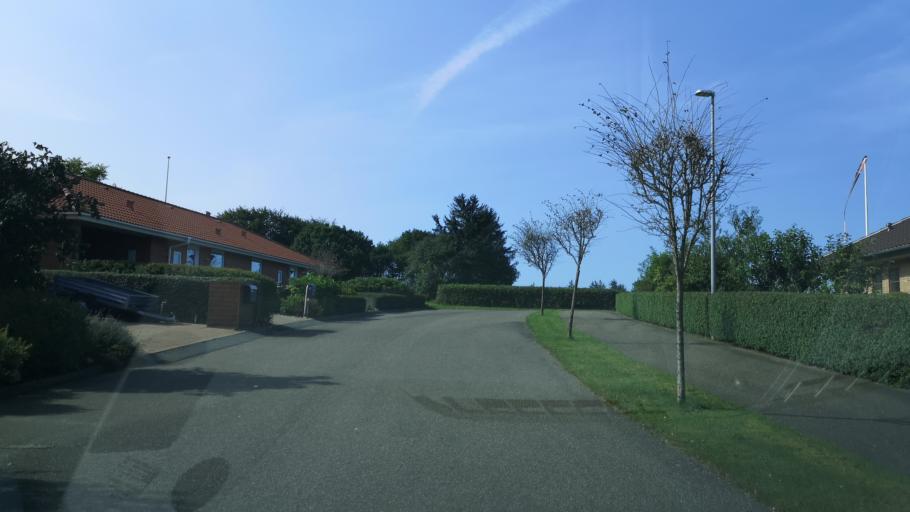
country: DK
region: Central Jutland
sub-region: Ringkobing-Skjern Kommune
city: Videbaek
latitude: 56.0853
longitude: 8.6148
